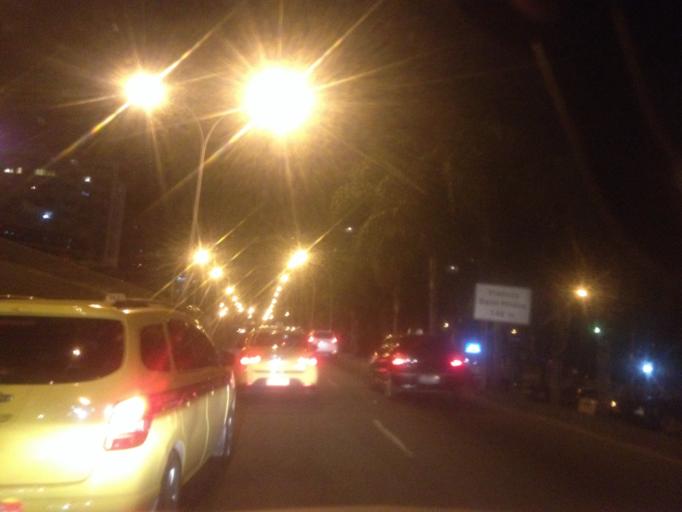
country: BR
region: Rio de Janeiro
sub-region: Rio De Janeiro
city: Rio de Janeiro
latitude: -22.9619
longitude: -43.2039
